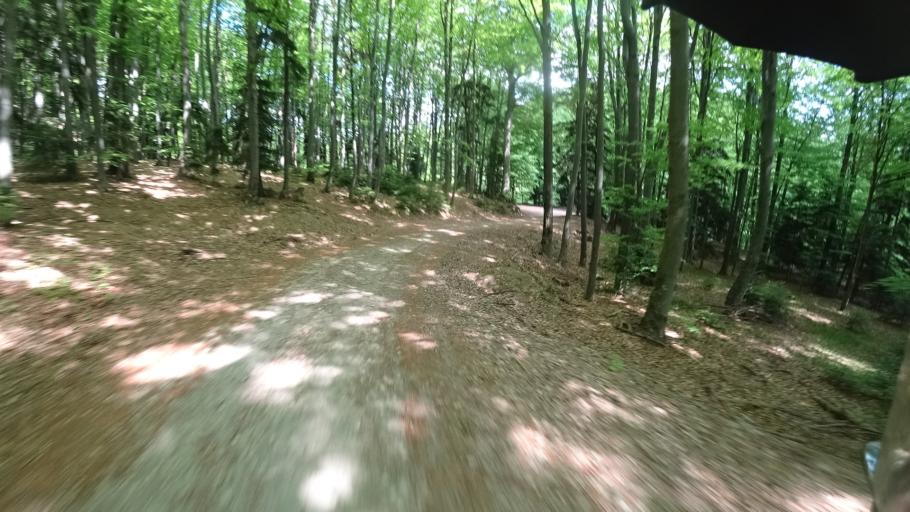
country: HR
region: Grad Zagreb
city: Kasina
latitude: 45.9236
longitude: 16.0202
